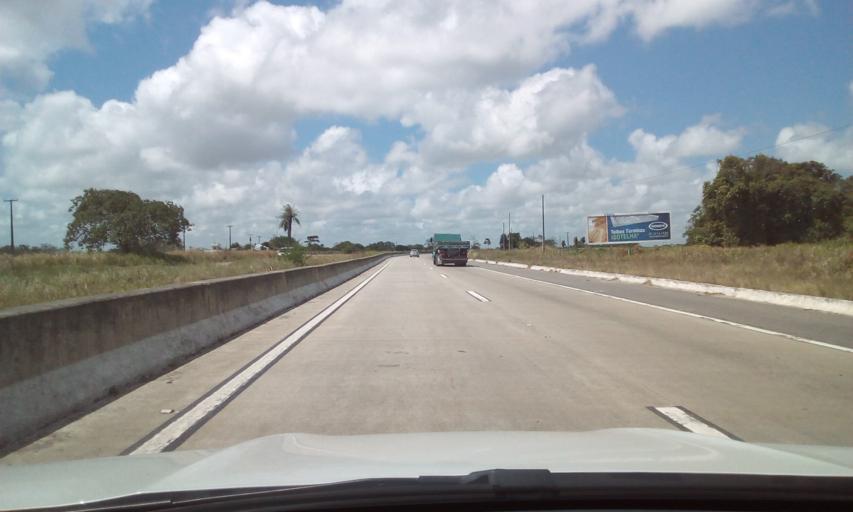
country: BR
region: Pernambuco
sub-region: Itapissuma
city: Itapissuma
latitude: -7.7251
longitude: -34.9420
